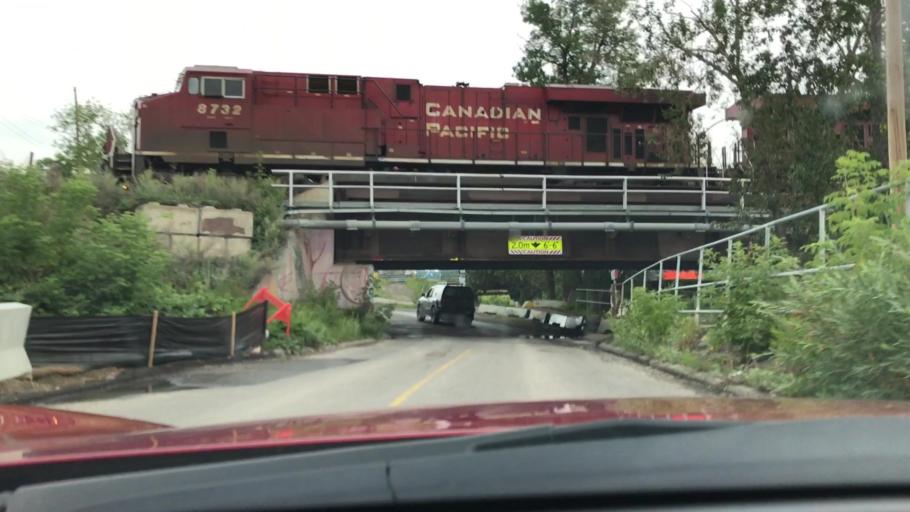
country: CA
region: Alberta
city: Calgary
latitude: 51.0430
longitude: -114.0436
